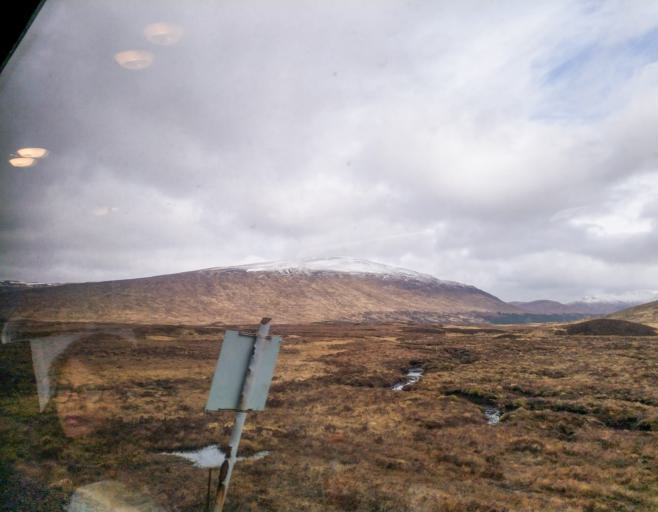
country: GB
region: Scotland
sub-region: Highland
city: Spean Bridge
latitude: 56.7509
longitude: -4.6767
